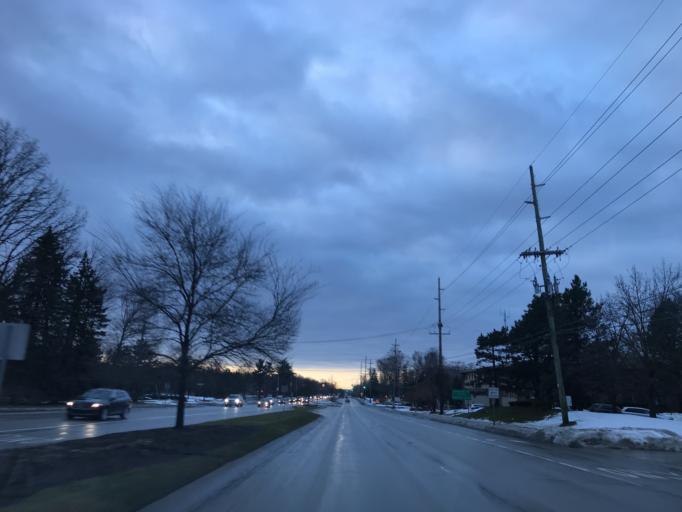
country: US
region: Michigan
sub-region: Oakland County
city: Farmington Hills
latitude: 42.4866
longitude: -83.3581
